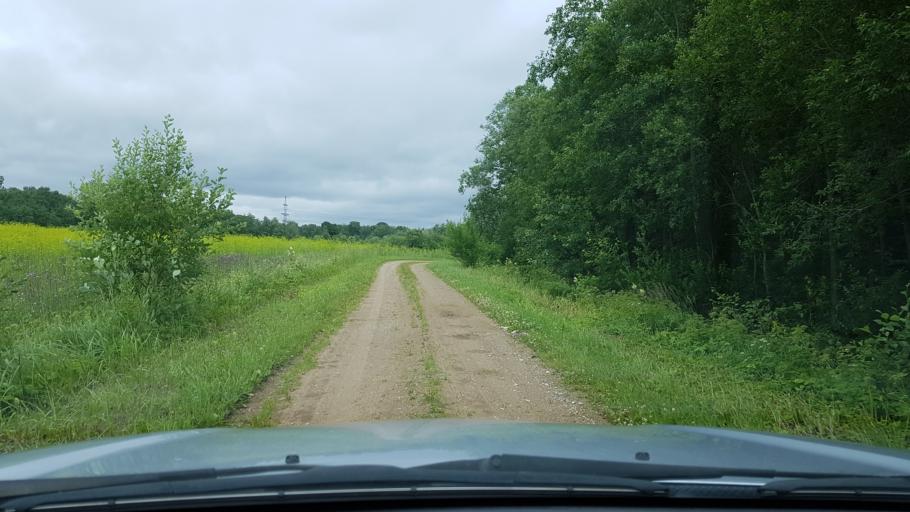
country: EE
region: Ida-Virumaa
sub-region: Narva-Joesuu linn
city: Narva-Joesuu
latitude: 59.3427
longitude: 27.9656
